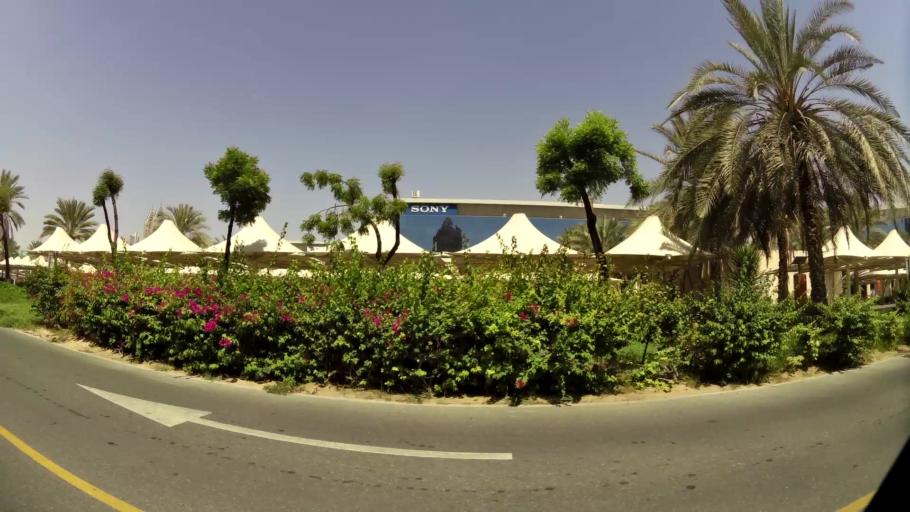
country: AE
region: Dubai
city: Dubai
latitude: 25.0950
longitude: 55.1587
